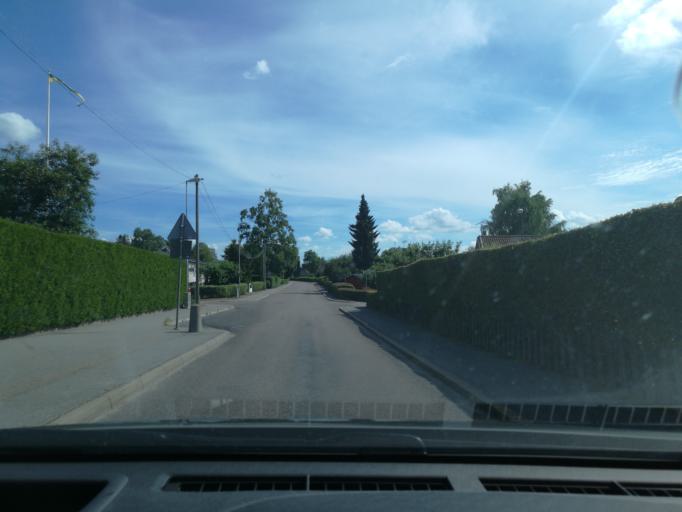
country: SE
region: Stockholm
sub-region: Upplands Vasby Kommun
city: Upplands Vaesby
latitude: 59.4801
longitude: 17.8959
